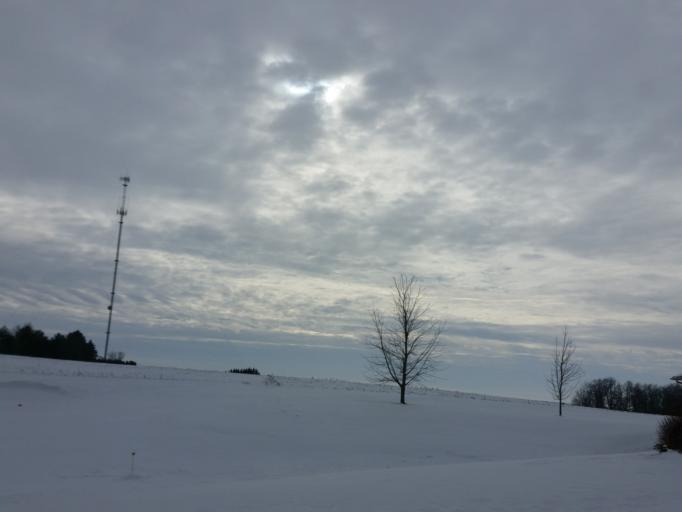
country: US
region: Iowa
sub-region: Dubuque County
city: Peosta
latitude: 42.3821
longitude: -90.7844
